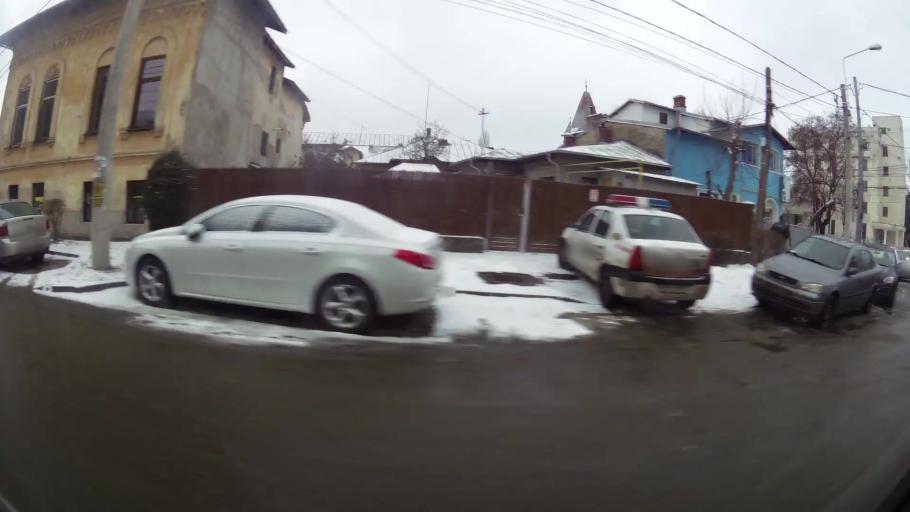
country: RO
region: Prahova
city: Ploiesti
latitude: 44.9364
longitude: 26.0301
